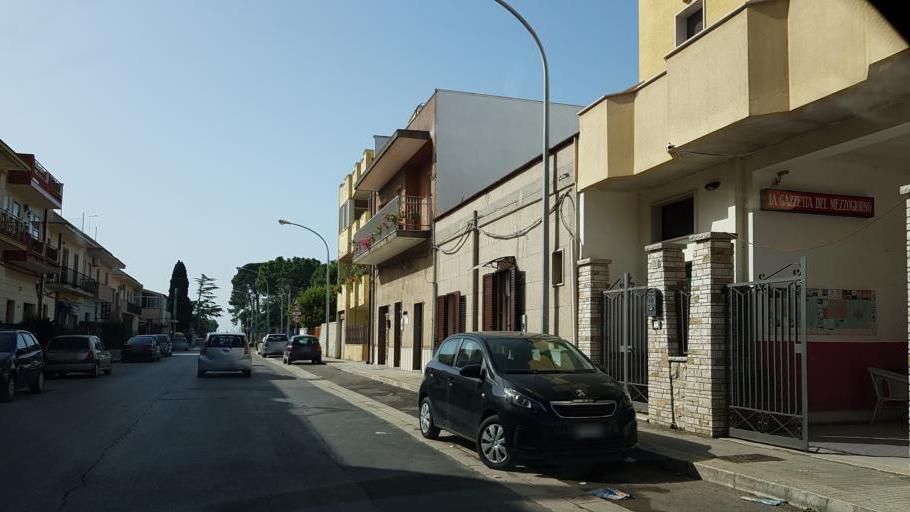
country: IT
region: Apulia
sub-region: Provincia di Brindisi
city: Mesagne
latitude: 40.5525
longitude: 17.8140
